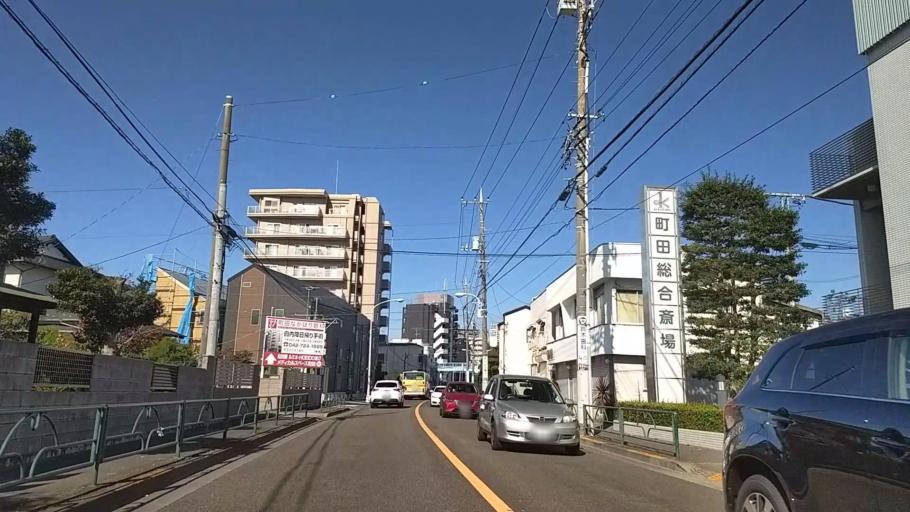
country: JP
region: Tokyo
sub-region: Machida-shi
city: Machida
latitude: 35.5352
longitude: 139.4576
